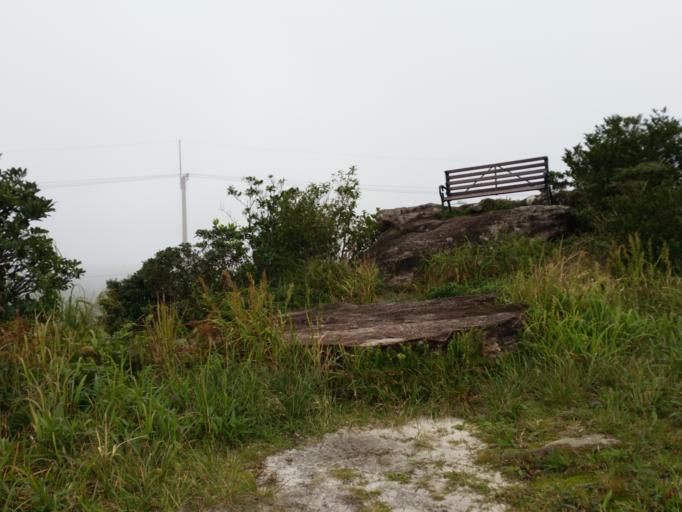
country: KH
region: Kampot
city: Kampot
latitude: 10.6269
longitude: 104.0229
